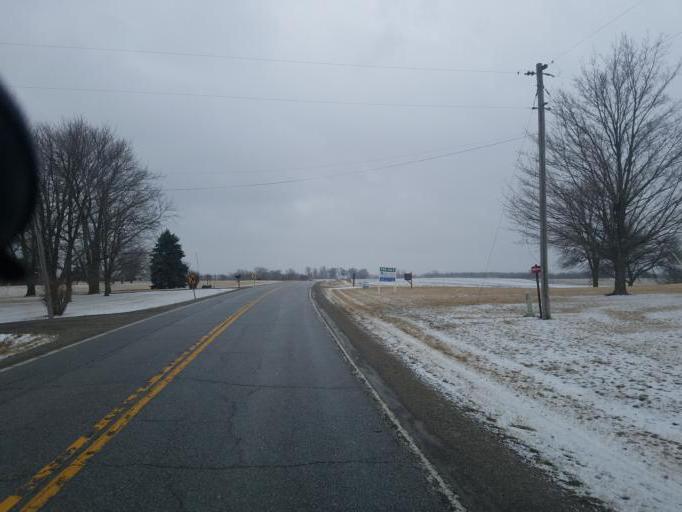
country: US
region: Missouri
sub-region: Putnam County
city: Unionville
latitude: 40.5088
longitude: -93.0093
